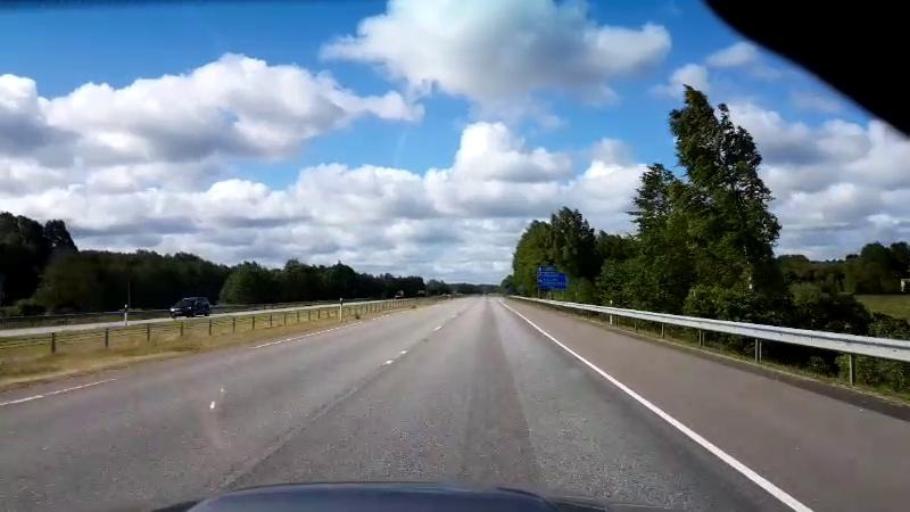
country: EE
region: Harju
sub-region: Saue linn
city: Saue
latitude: 59.2668
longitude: 24.5152
